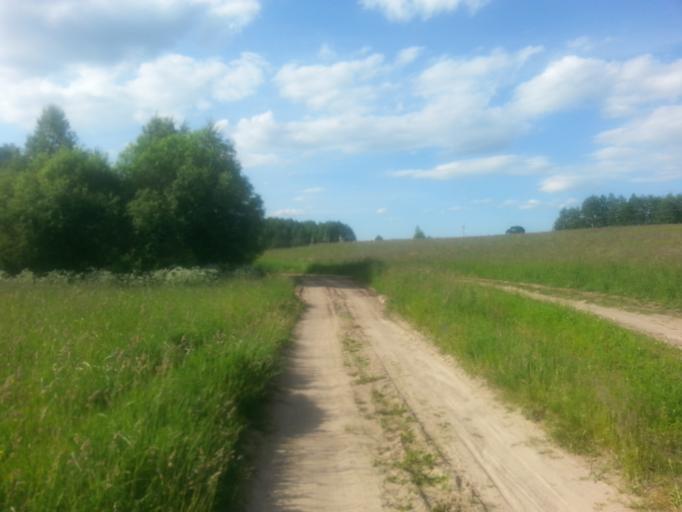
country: BY
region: Minsk
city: Narach
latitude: 54.9731
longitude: 26.6128
